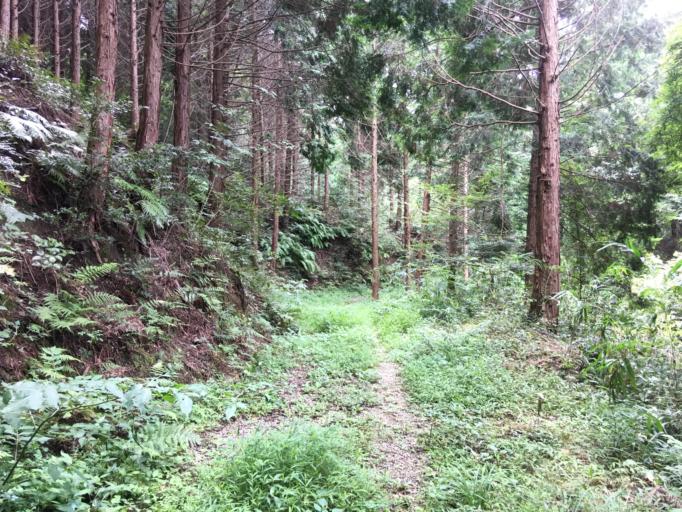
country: JP
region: Nara
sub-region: Ikoma-shi
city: Ikoma
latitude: 34.6998
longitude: 135.6684
